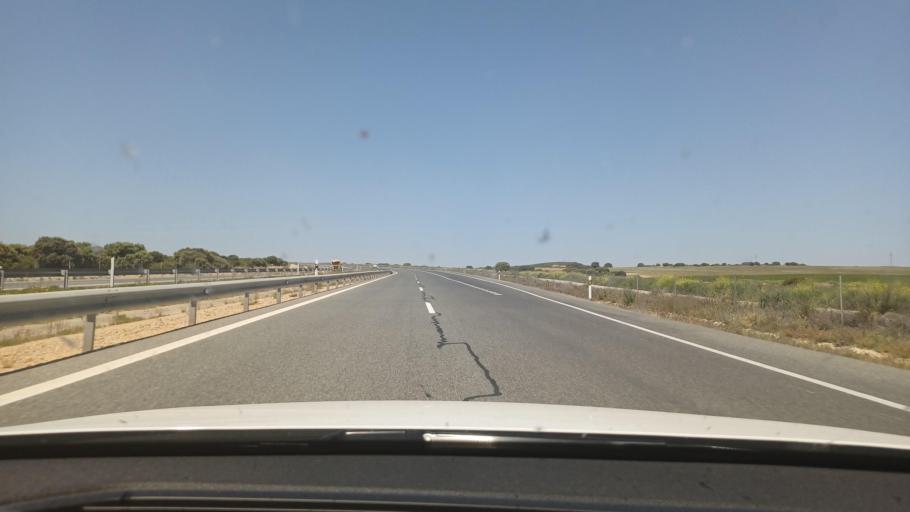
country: ES
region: Castille-La Mancha
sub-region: Provincia de Albacete
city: Corral-Rubio
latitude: 38.8956
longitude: -1.4265
